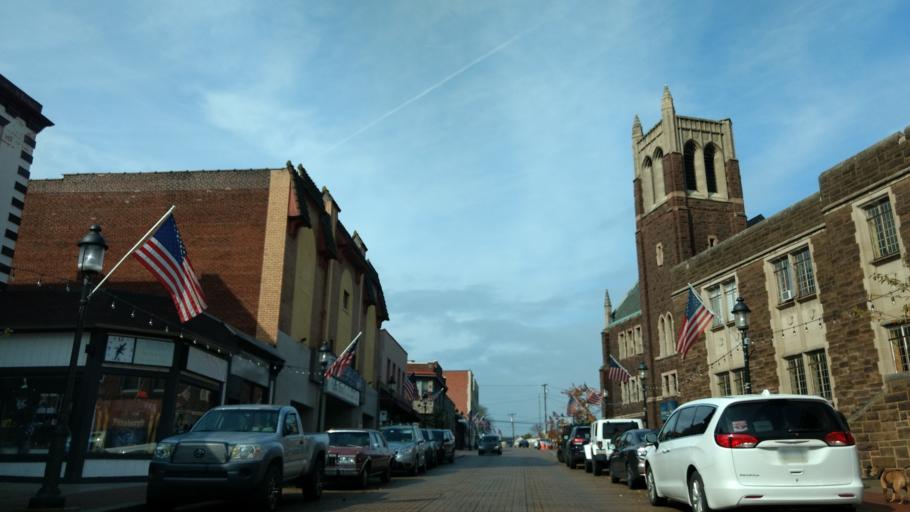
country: US
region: Pennsylvania
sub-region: Allegheny County
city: Dormont
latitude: 40.3959
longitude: -80.0350
